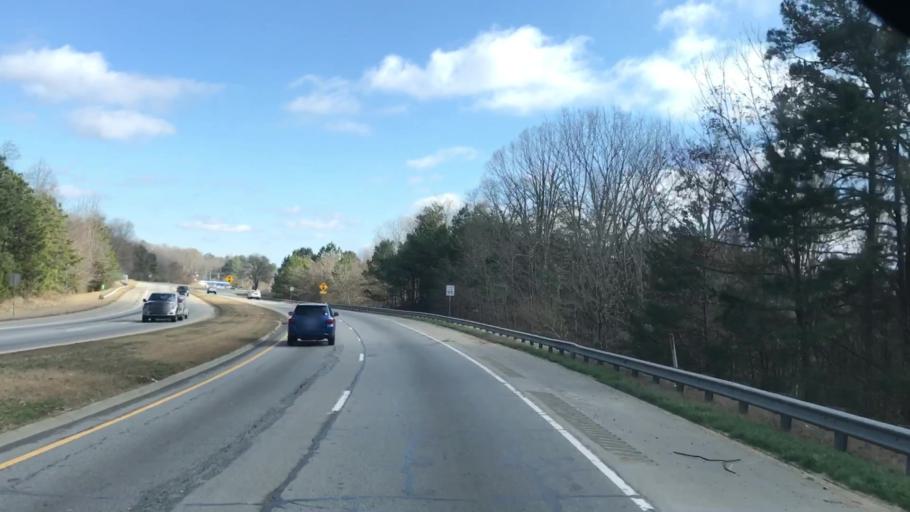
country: US
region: Georgia
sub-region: Hall County
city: Gainesville
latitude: 34.2815
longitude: -83.7970
